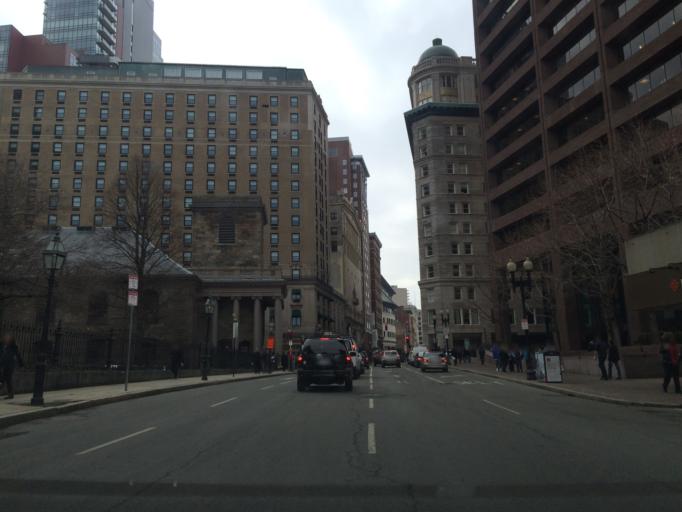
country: US
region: Massachusetts
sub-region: Suffolk County
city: Boston
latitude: 42.3587
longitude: -71.0601
